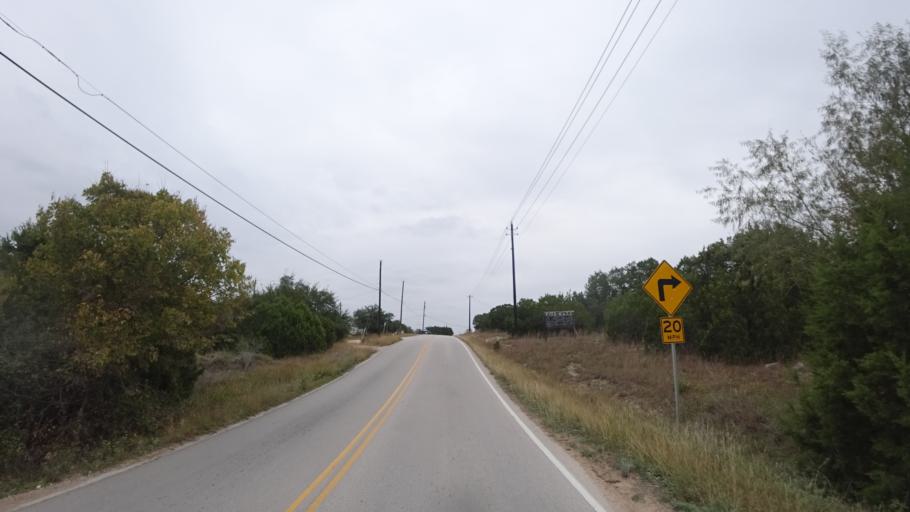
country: US
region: Texas
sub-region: Travis County
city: Lakeway
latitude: 30.3758
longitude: -97.9416
